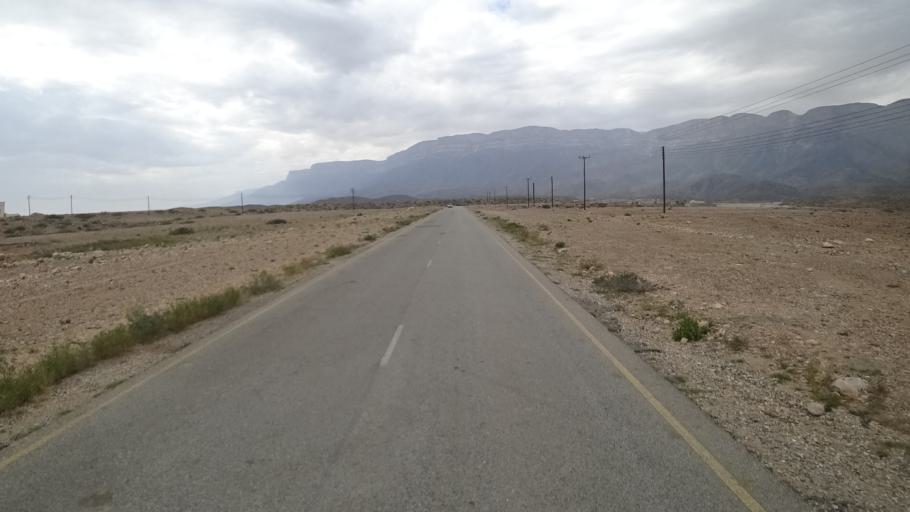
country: OM
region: Zufar
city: Salalah
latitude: 17.1549
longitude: 55.0009
